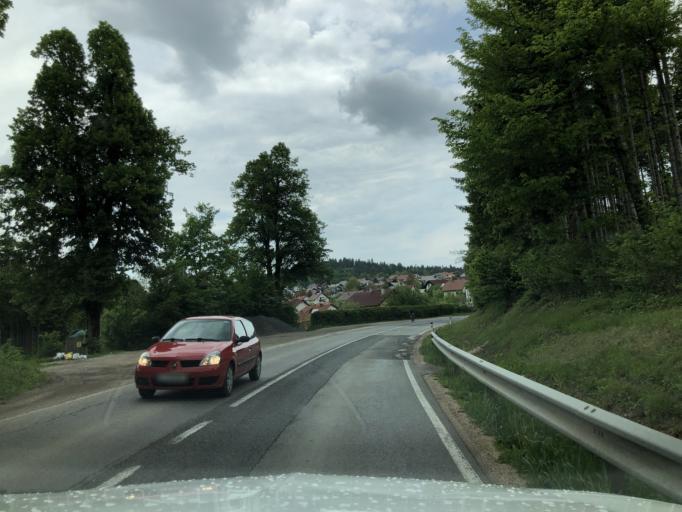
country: SI
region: Cerknica
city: Rakek
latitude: 45.8063
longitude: 14.3282
